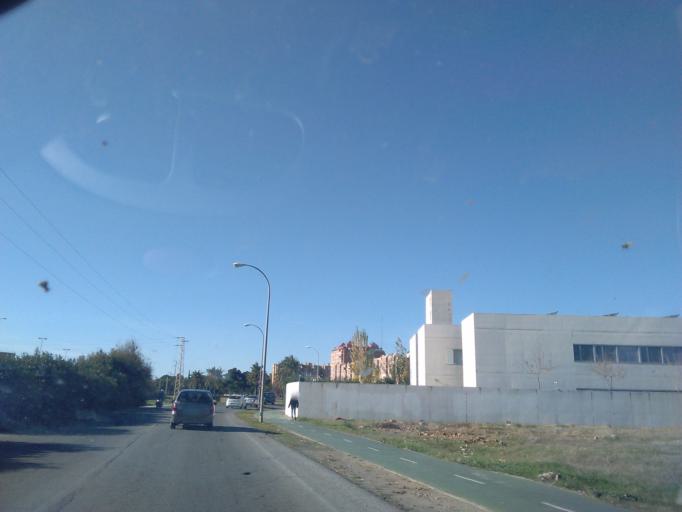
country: ES
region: Andalusia
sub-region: Provincia de Sevilla
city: Sevilla
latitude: 37.3860
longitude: -5.9156
